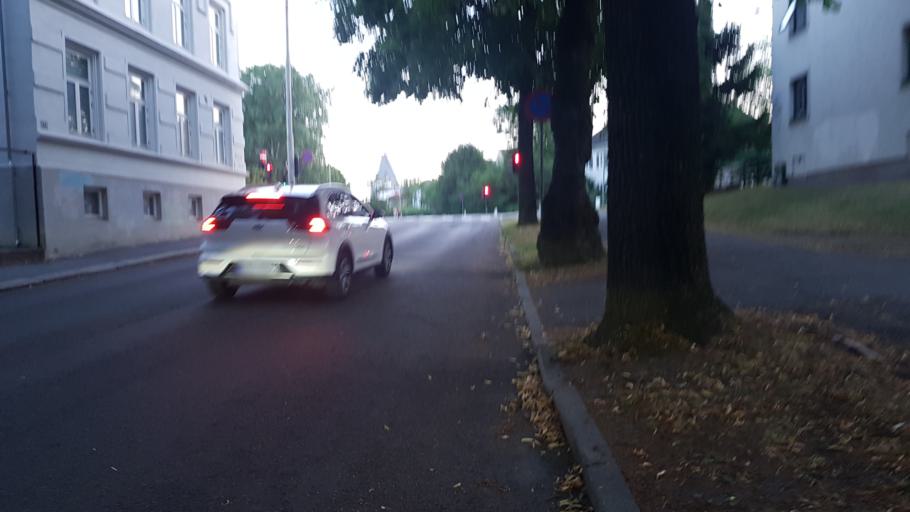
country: NO
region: Oslo
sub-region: Oslo
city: Oslo
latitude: 59.9302
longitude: 10.7444
